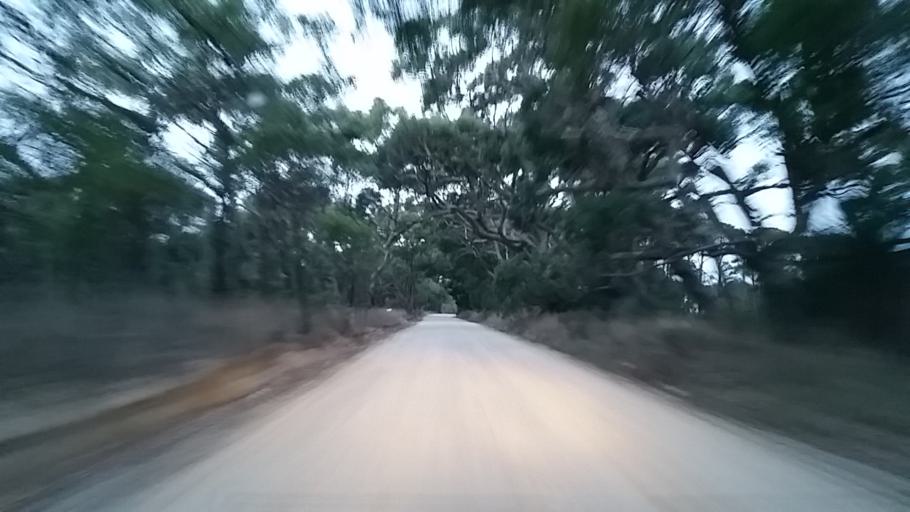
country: AU
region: South Australia
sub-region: Yankalilla
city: Normanville
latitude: -35.6107
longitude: 138.1663
